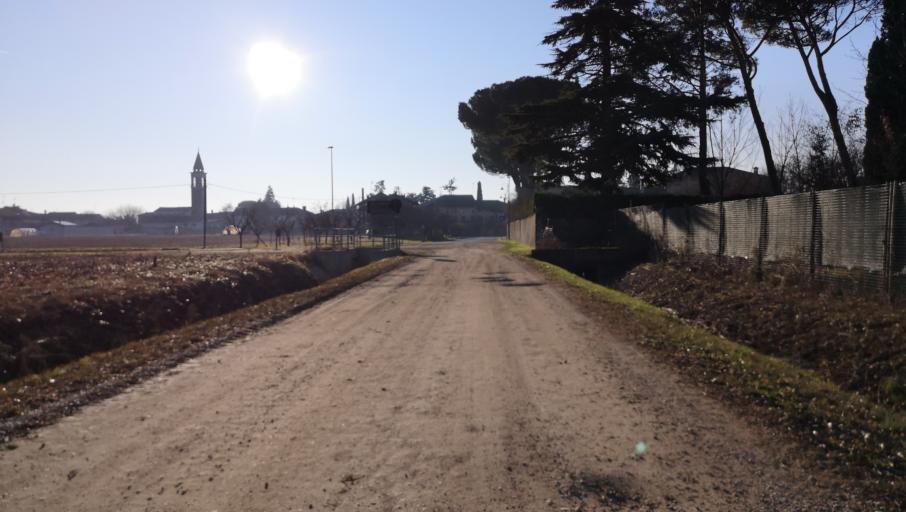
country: IT
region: Friuli Venezia Giulia
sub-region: Provincia di Udine
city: Lauzacco
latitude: 45.9673
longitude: 13.2957
